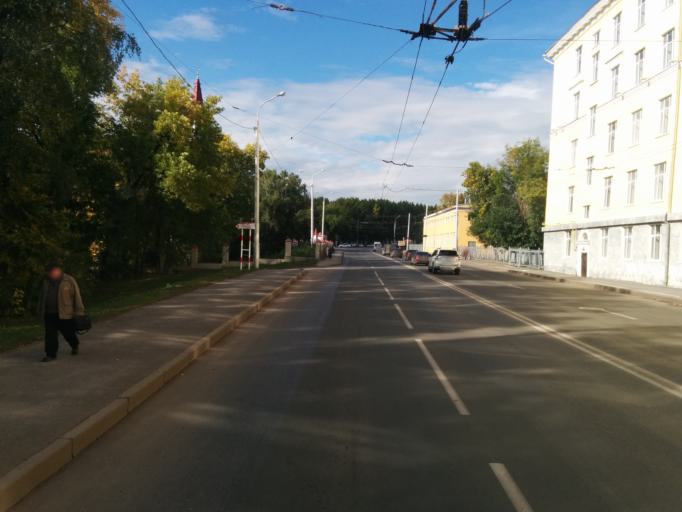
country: RU
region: Bashkortostan
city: Ufa
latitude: 54.8183
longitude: 56.0573
